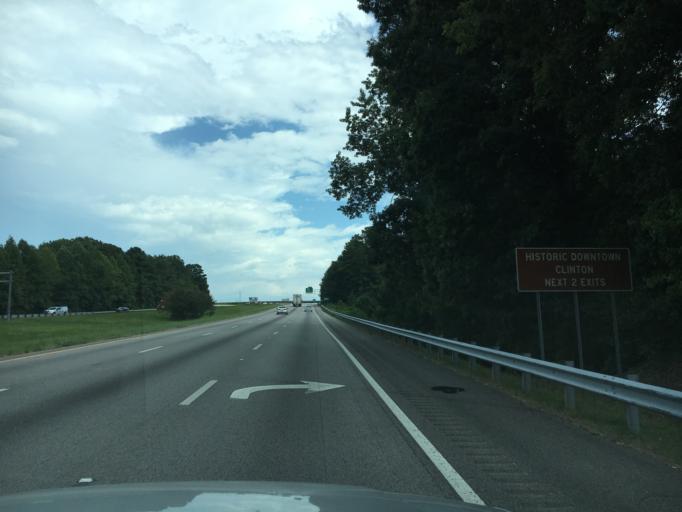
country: US
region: South Carolina
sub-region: Laurens County
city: Clinton
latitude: 34.5093
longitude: -81.8648
